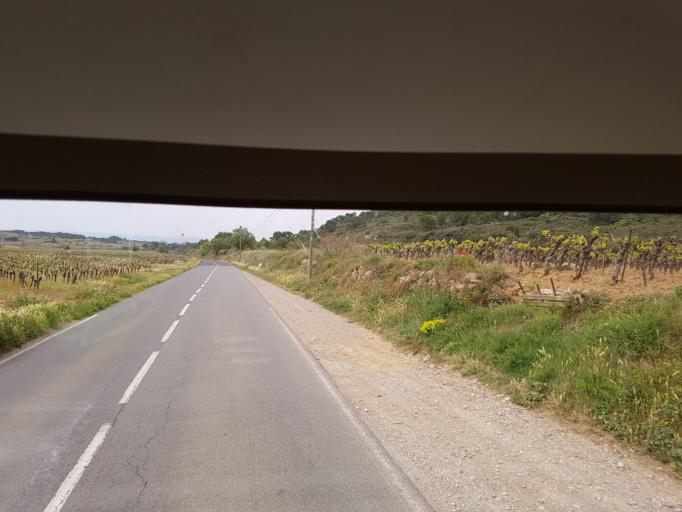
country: FR
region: Languedoc-Roussillon
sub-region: Departement de l'Aude
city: Fleury
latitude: 43.2111
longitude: 3.1370
